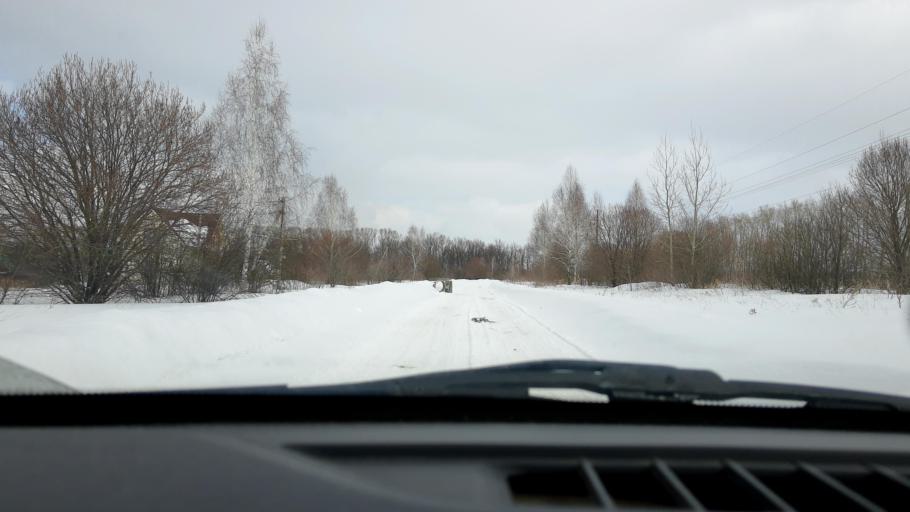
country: RU
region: Bashkortostan
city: Iglino
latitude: 54.7299
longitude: 56.2334
